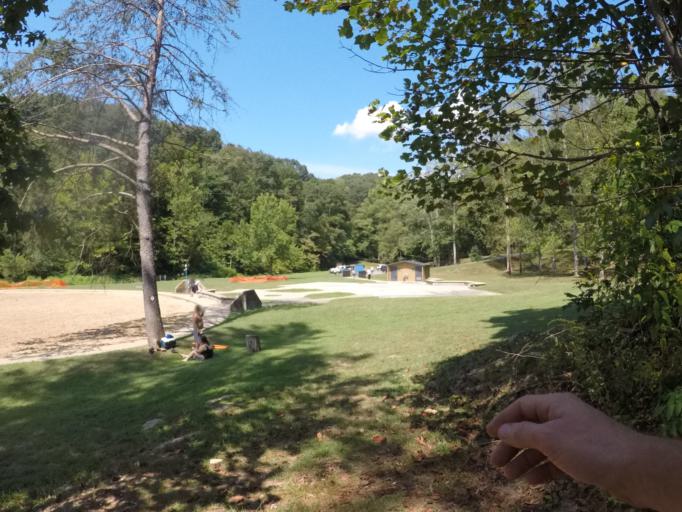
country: US
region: Ohio
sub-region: Lawrence County
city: Ironton
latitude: 38.6197
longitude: -82.6282
